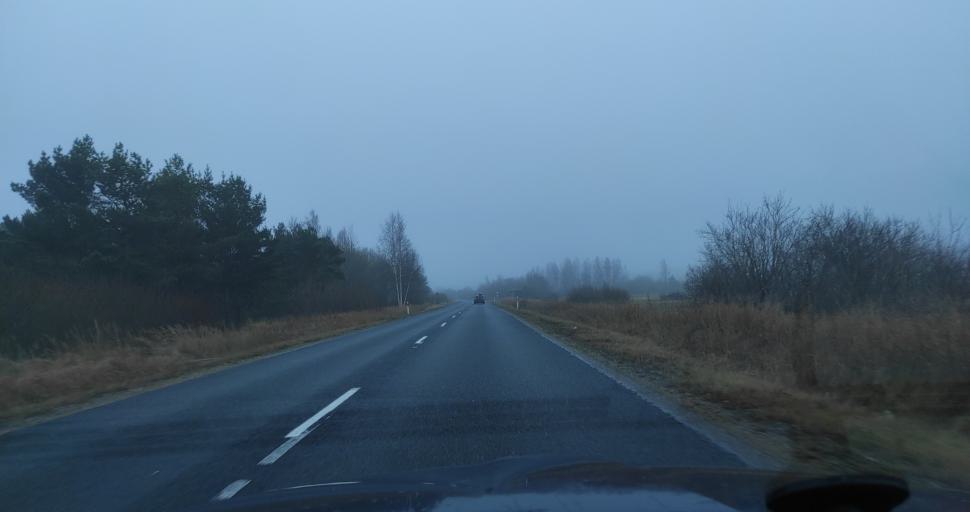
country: LV
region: Alsunga
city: Alsunga
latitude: 57.1166
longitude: 21.4239
